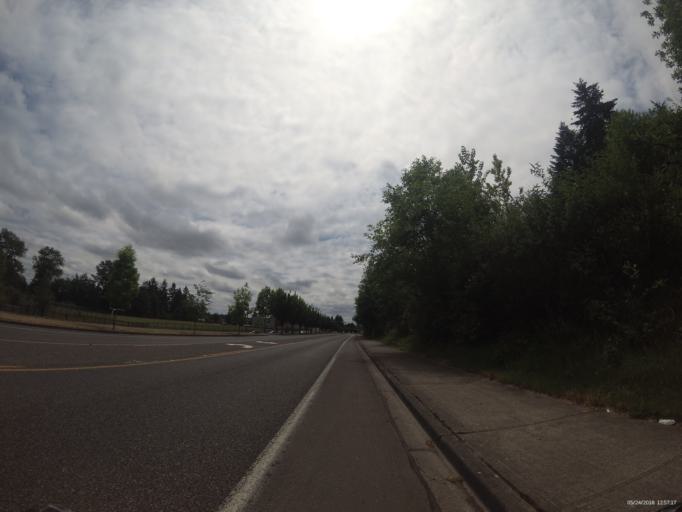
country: US
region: Washington
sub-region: Pierce County
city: Lakewood
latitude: 47.2024
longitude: -122.4927
